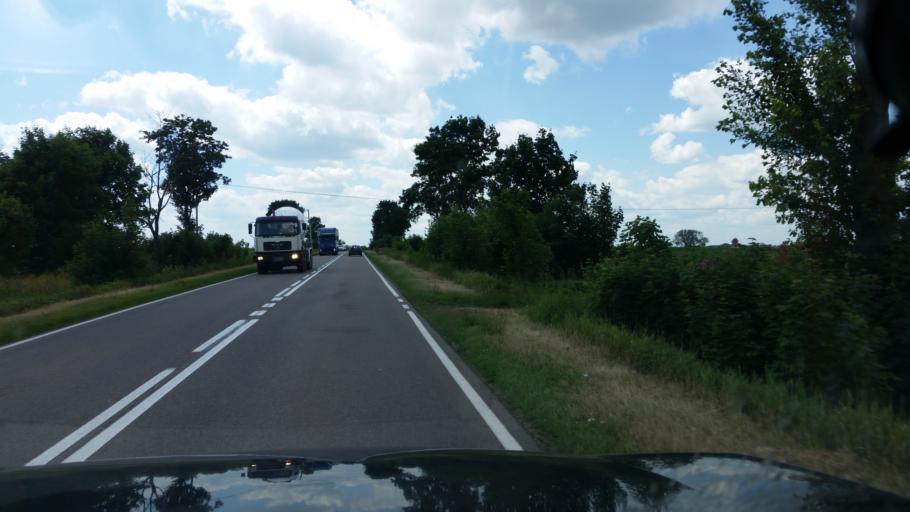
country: PL
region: Podlasie
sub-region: Powiat lomzynski
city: Sniadowo
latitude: 53.0124
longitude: 21.9468
